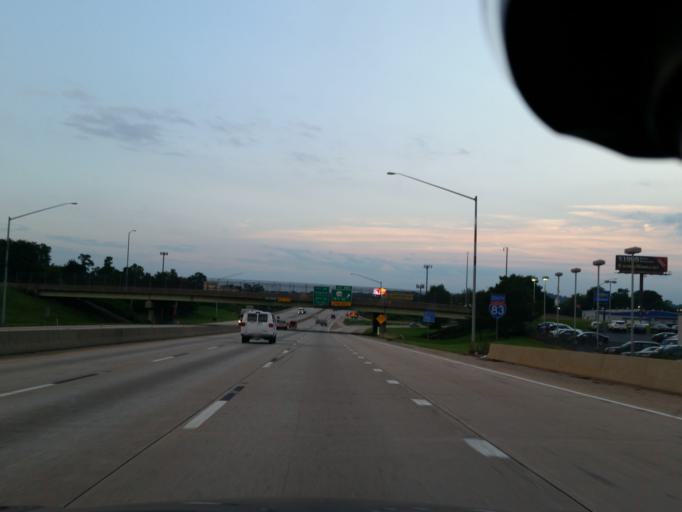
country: US
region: Pennsylvania
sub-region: Dauphin County
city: Penbrook
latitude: 40.2550
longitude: -76.8630
